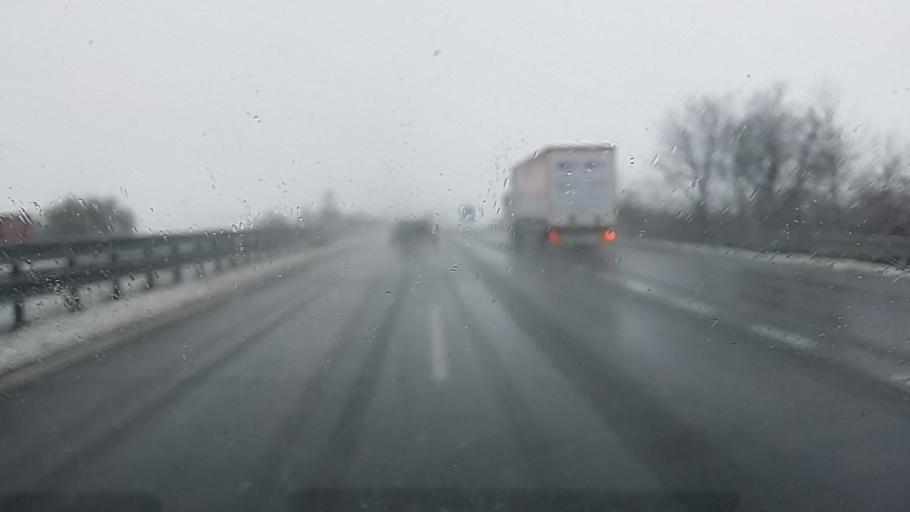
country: CZ
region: South Moravian
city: Hrusky
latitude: 48.7828
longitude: 16.9259
